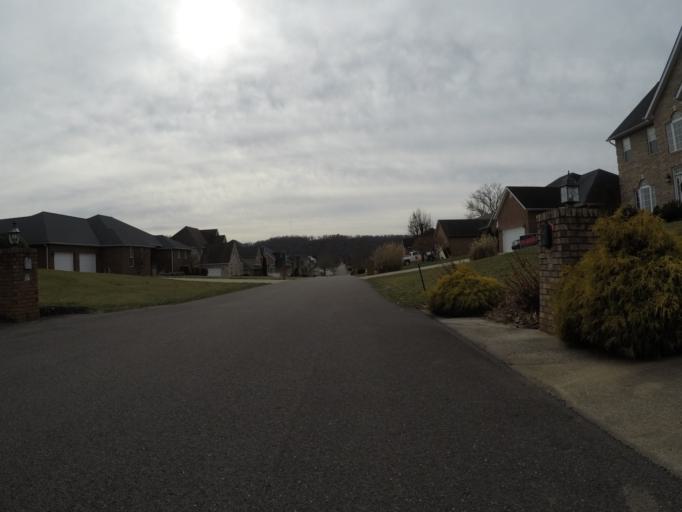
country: US
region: West Virginia
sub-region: Cabell County
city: Pea Ridge
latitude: 38.4480
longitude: -82.3495
